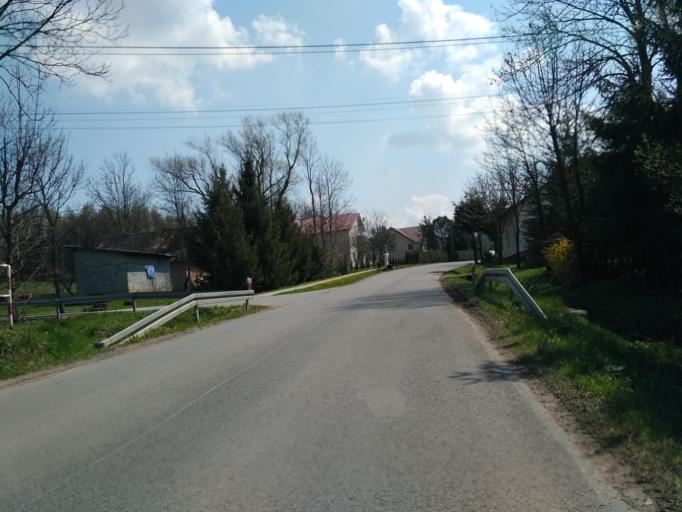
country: PL
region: Subcarpathian Voivodeship
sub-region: Powiat sanocki
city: Bukowsko
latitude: 49.5021
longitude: 22.0345
